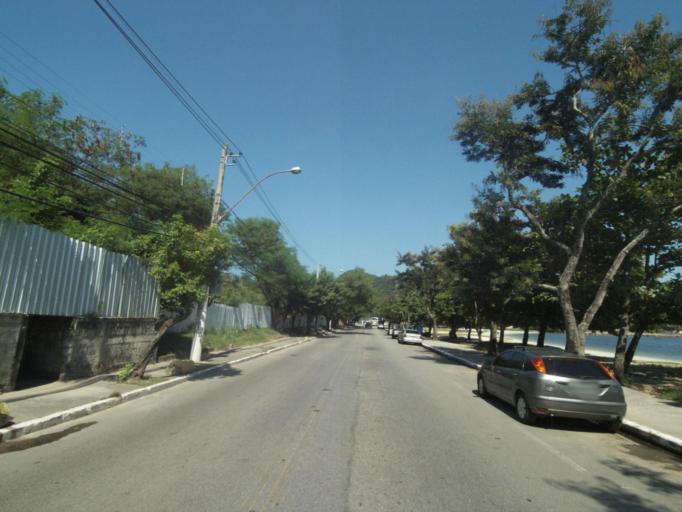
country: BR
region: Rio de Janeiro
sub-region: Niteroi
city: Niteroi
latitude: -22.9355
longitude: -43.1037
